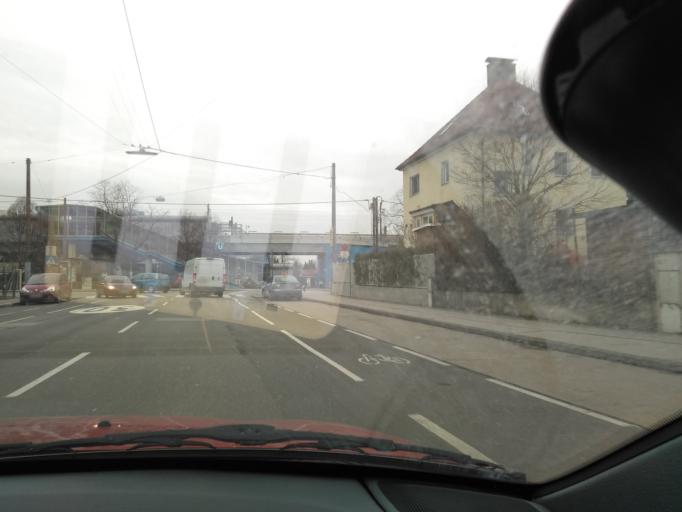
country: AT
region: Lower Austria
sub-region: Politischer Bezirk Modling
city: Vosendorf
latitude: 48.1604
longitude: 16.3227
